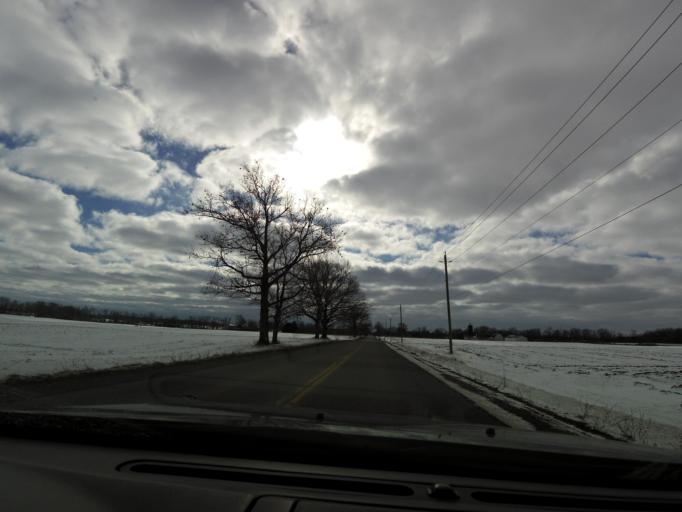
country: CA
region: Ontario
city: Hamilton
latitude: 43.1239
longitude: -79.6546
